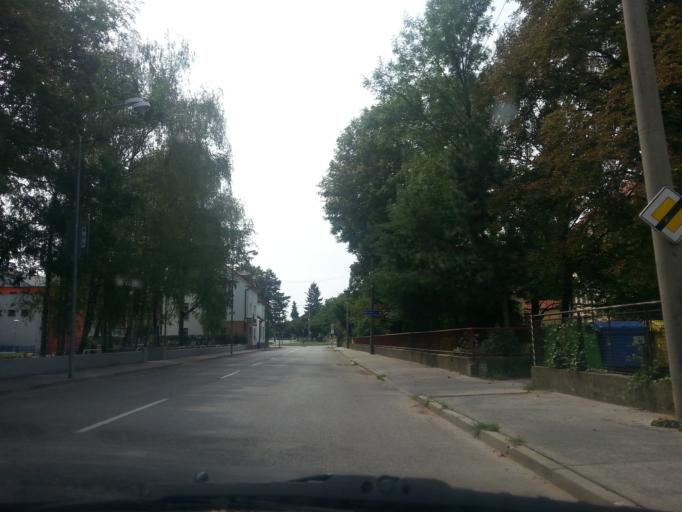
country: SK
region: Trenciansky
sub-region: Okres Nove Mesto nad Vahom
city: Nove Mesto nad Vahom
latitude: 48.7581
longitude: 17.8256
